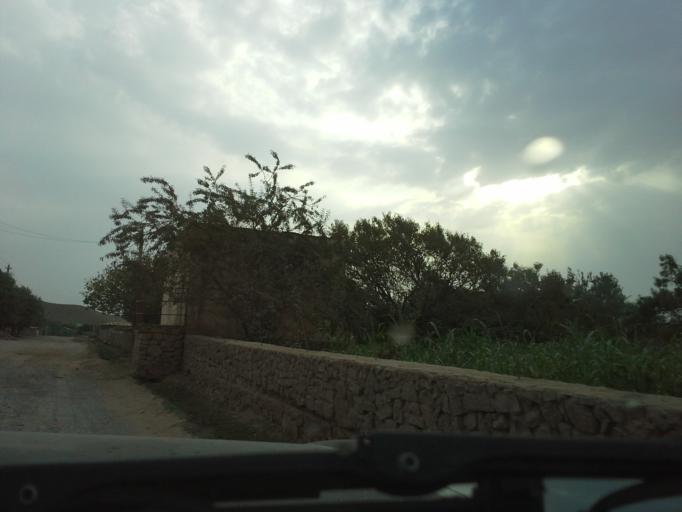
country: UZ
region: Qashqadaryo
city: Qorashina
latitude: 37.9294
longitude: 66.4961
